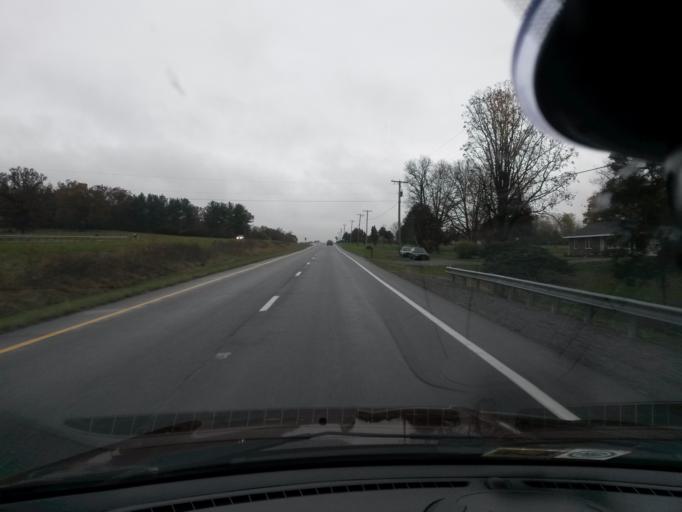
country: US
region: Virginia
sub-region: Botetourt County
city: Fincastle
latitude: 37.5282
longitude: -79.8727
